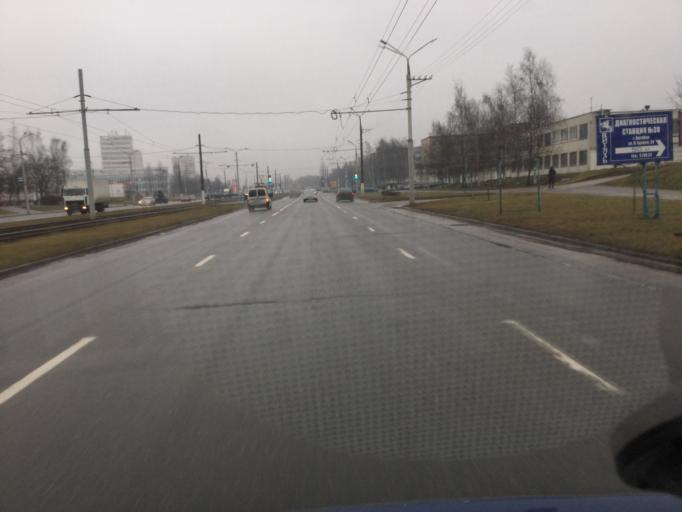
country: BY
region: Vitebsk
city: Vitebsk
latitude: 55.1622
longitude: 30.2376
